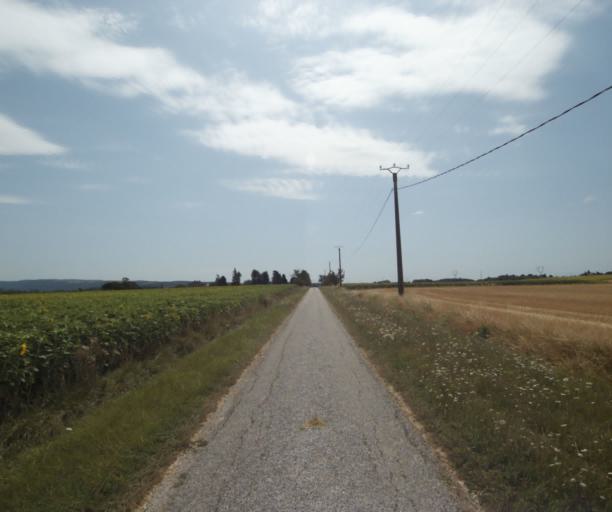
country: FR
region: Midi-Pyrenees
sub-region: Departement de la Haute-Garonne
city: Saint-Felix-Lauragais
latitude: 43.4213
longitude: 1.9114
